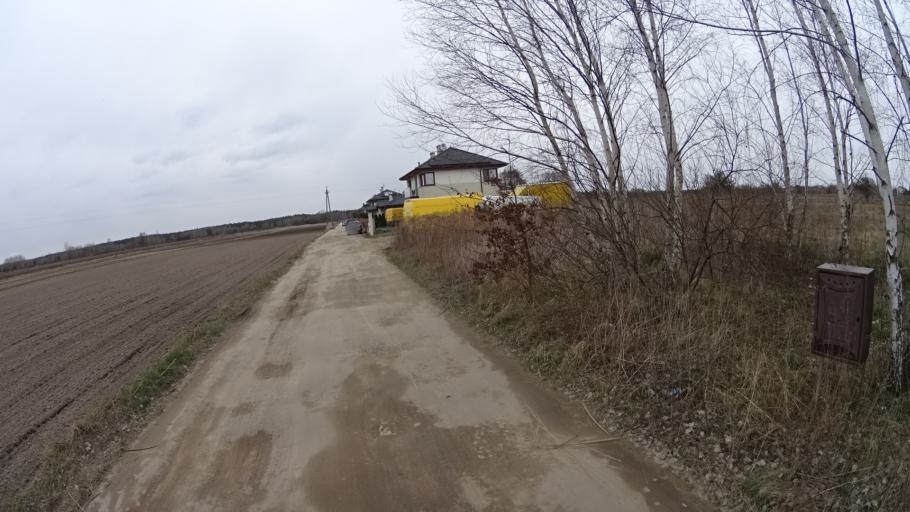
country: PL
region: Masovian Voivodeship
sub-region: Powiat warszawski zachodni
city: Hornowek
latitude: 52.2667
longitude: 20.7895
